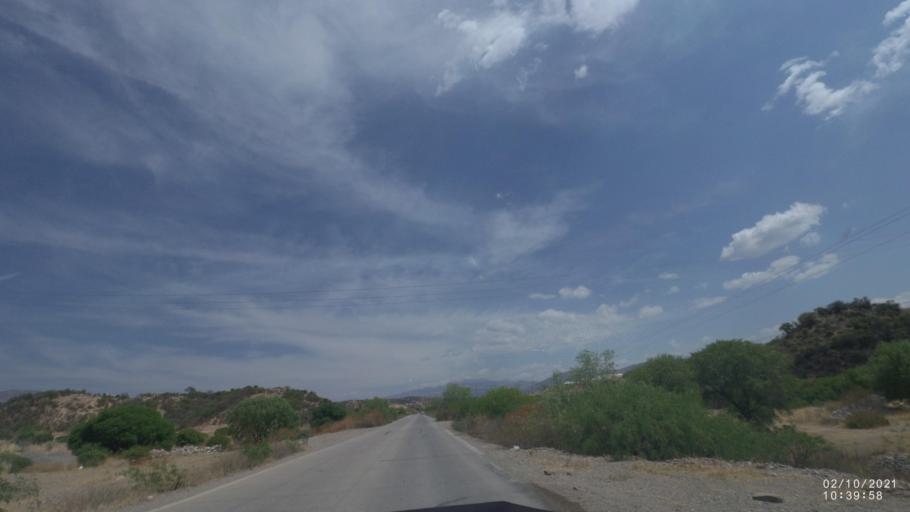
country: BO
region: Cochabamba
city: Capinota
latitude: -17.6261
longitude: -66.2808
